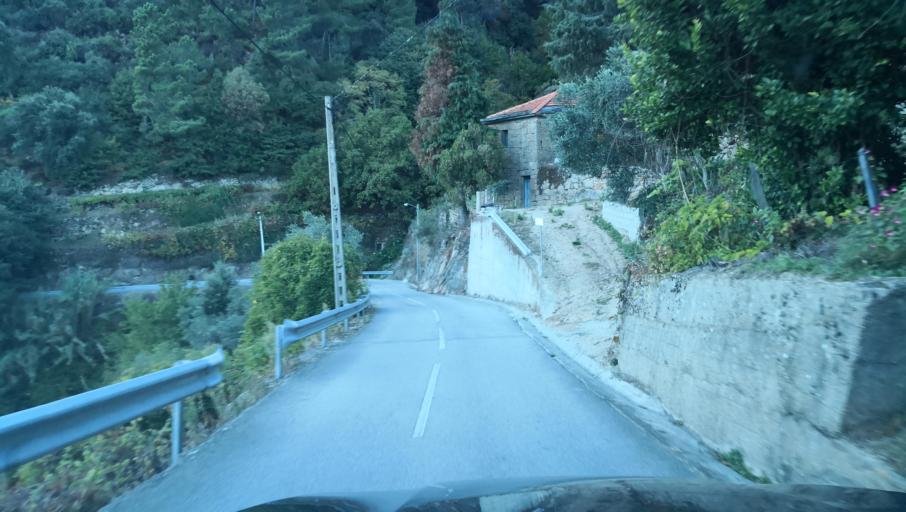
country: PT
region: Vila Real
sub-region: Santa Marta de Penaguiao
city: Santa Marta de Penaguiao
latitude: 41.2562
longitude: -7.8052
